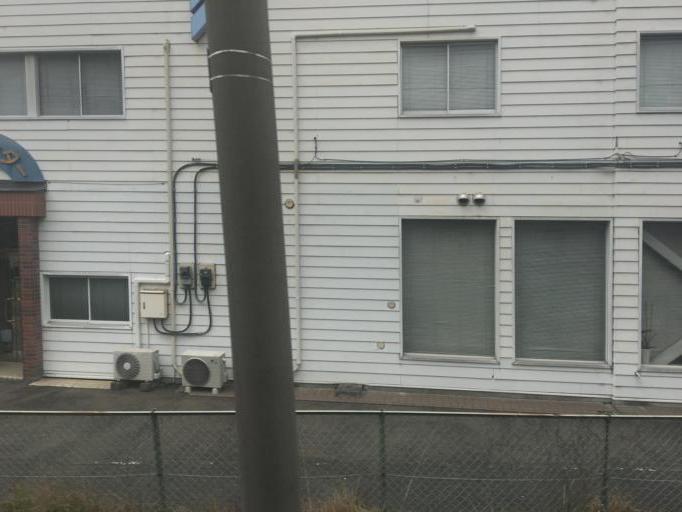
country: JP
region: Saitama
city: Sakado
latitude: 35.9378
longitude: 139.4225
